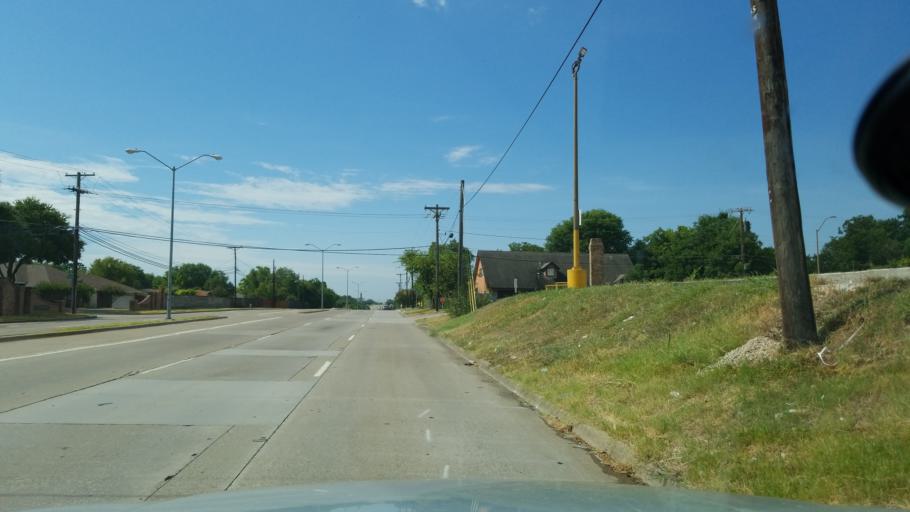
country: US
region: Texas
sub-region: Dallas County
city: Duncanville
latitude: 32.6703
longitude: -96.8572
